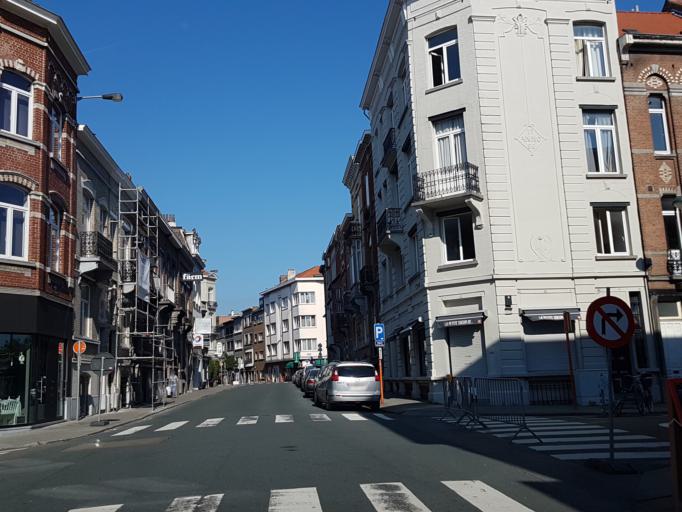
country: BE
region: Brussels Capital
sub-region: Bruxelles-Capitale
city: Brussels
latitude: 50.8418
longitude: 4.4014
